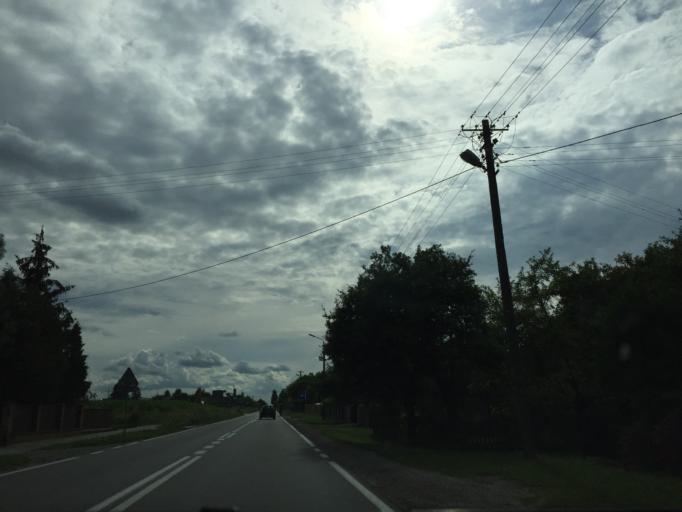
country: PL
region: Lublin Voivodeship
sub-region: Powiat lukowski
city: Trzebieszow
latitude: 51.9854
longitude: 22.5384
